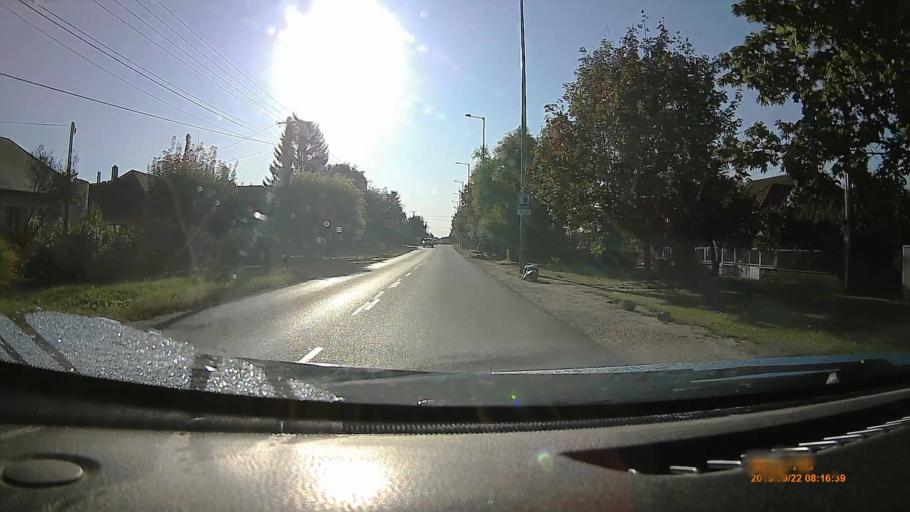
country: HU
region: Borsod-Abauj-Zemplen
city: Sajobabony
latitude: 48.1126
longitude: 20.6670
